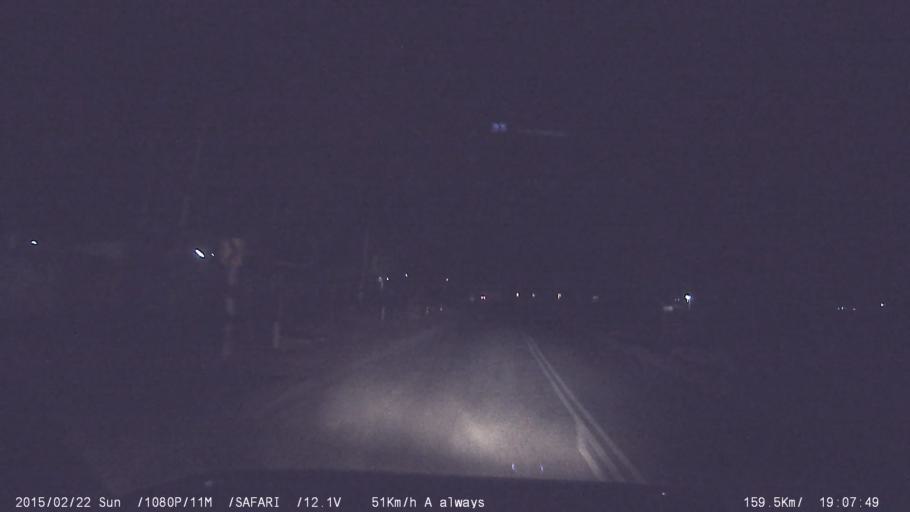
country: IN
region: Tamil Nadu
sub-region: Theni
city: Teni
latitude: 10.0477
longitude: 77.4998
